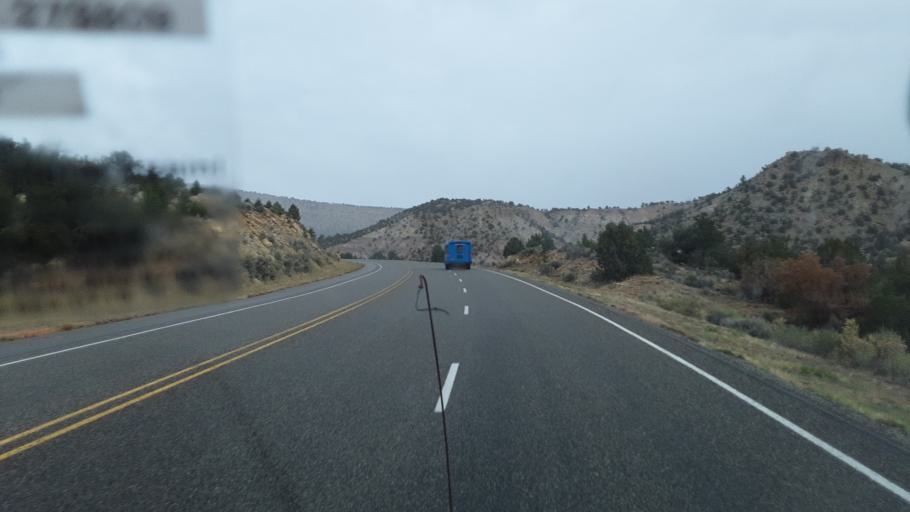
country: US
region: New Mexico
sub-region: Rio Arriba County
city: Santa Teresa
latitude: 36.3920
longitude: -106.4905
